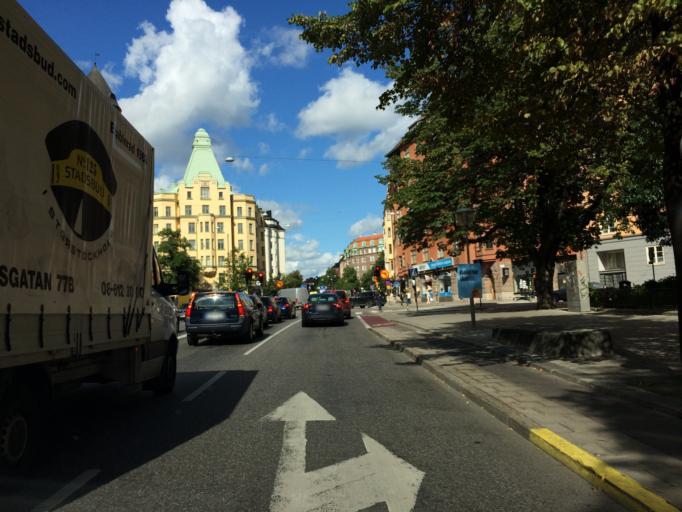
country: SE
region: Stockholm
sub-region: Stockholms Kommun
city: Stockholm
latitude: 59.3406
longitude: 18.0373
